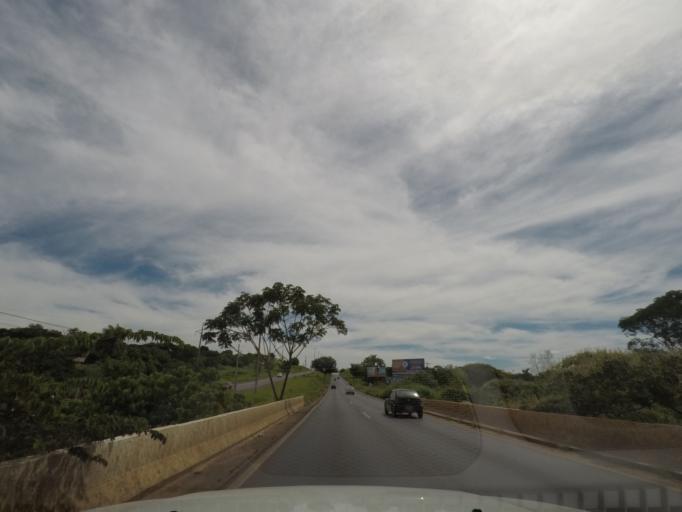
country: BR
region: Goias
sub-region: Planaltina
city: Planaltina
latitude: -15.6074
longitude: -47.6913
